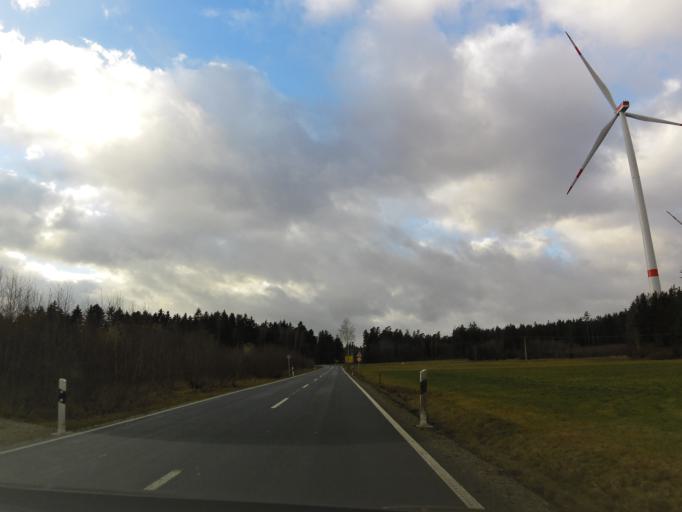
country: DE
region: Bavaria
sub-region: Upper Franconia
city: Hochstadt bei Thiersheim
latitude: 50.0742
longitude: 12.0918
